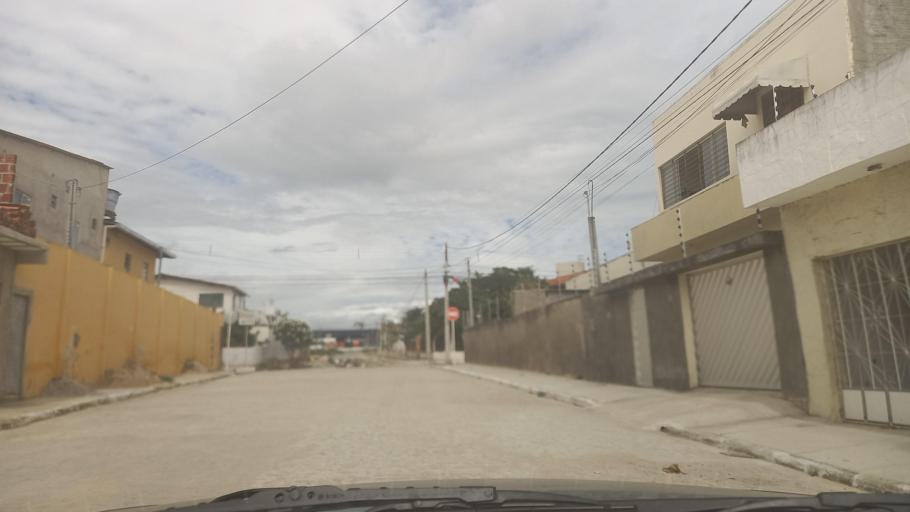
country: BR
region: Pernambuco
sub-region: Caruaru
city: Caruaru
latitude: -8.2926
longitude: -35.9911
